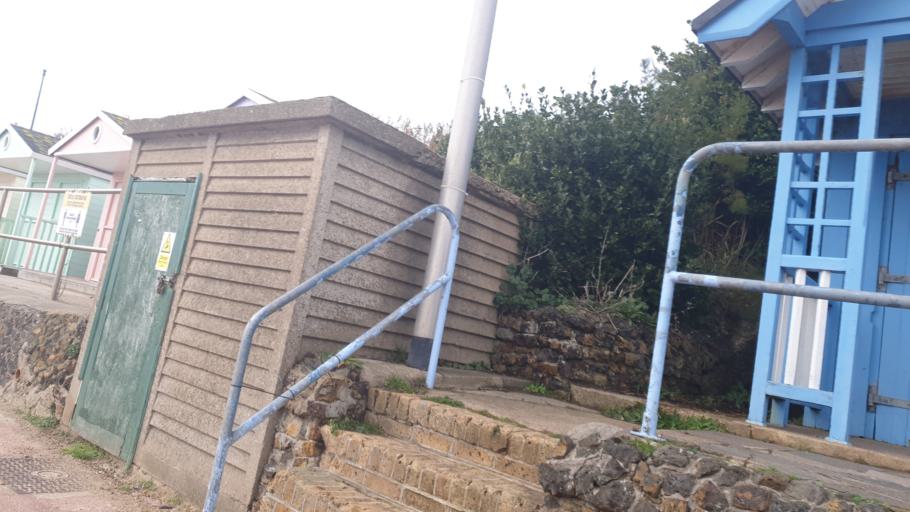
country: GB
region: England
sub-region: Essex
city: Clacton-on-Sea
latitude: 51.7836
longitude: 1.1473
